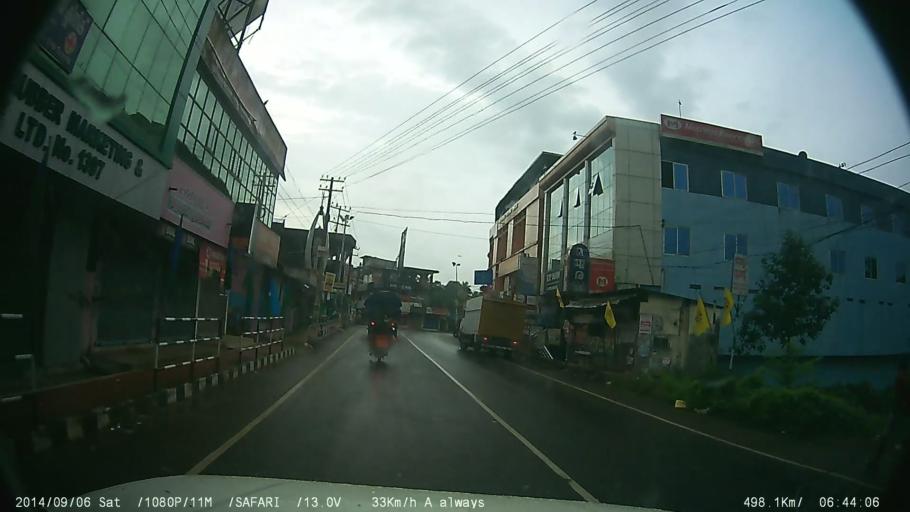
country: IN
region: Kerala
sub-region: Kottayam
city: Vaikam
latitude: 9.7683
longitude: 76.4898
